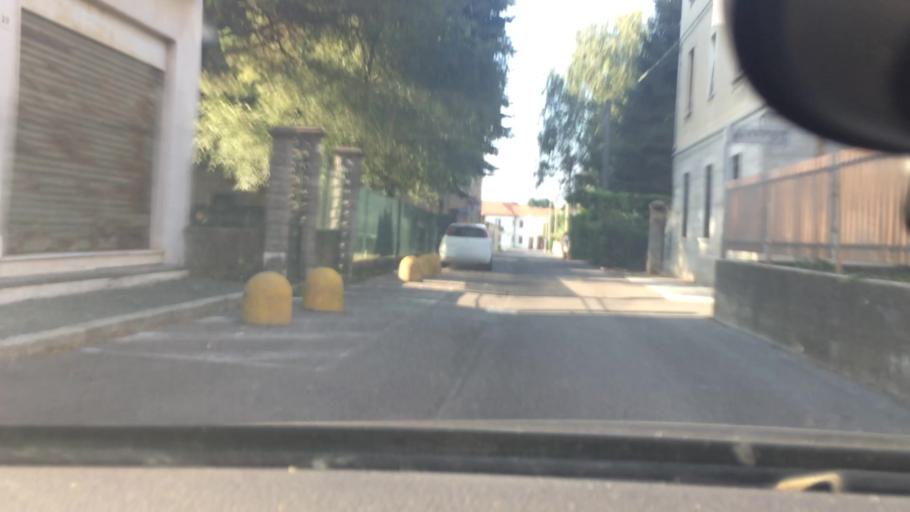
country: IT
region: Lombardy
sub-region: Provincia di Varese
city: Gerenzano
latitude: 45.6489
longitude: 9.0001
